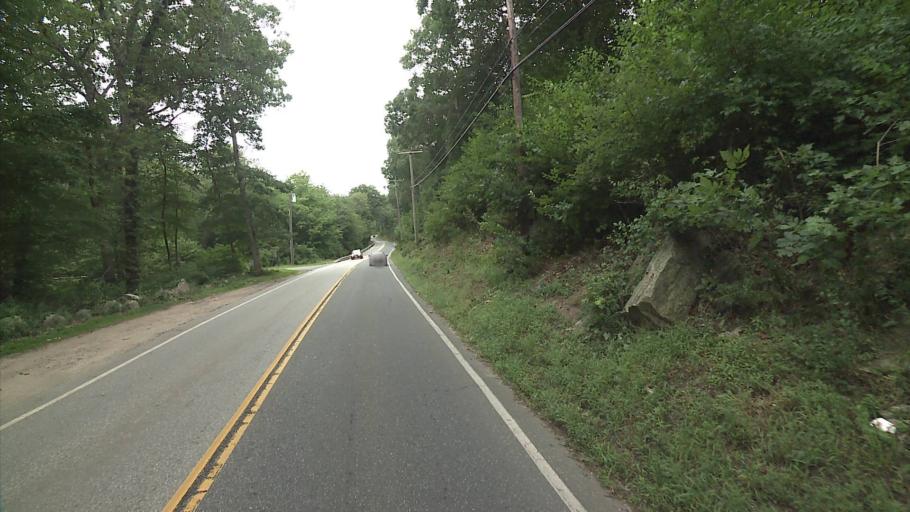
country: US
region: Connecticut
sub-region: New London County
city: Niantic
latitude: 41.3017
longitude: -72.2578
